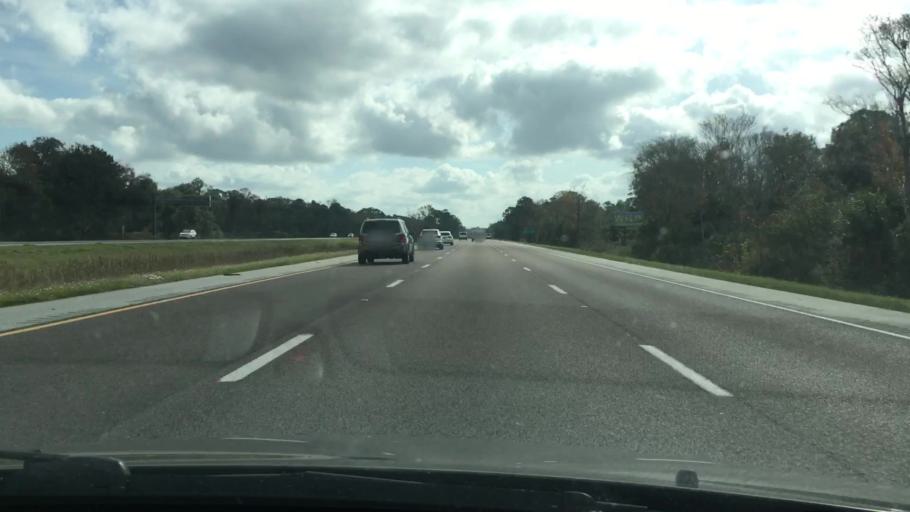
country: US
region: Florida
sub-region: Volusia County
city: Edgewater
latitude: 28.9399
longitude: -80.9460
